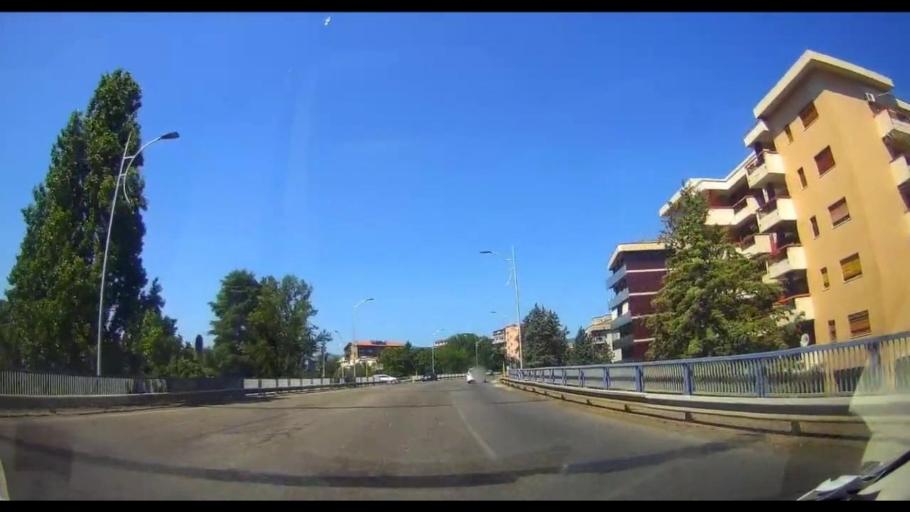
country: IT
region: Calabria
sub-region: Provincia di Cosenza
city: Cosenza
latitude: 39.3106
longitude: 16.2529
